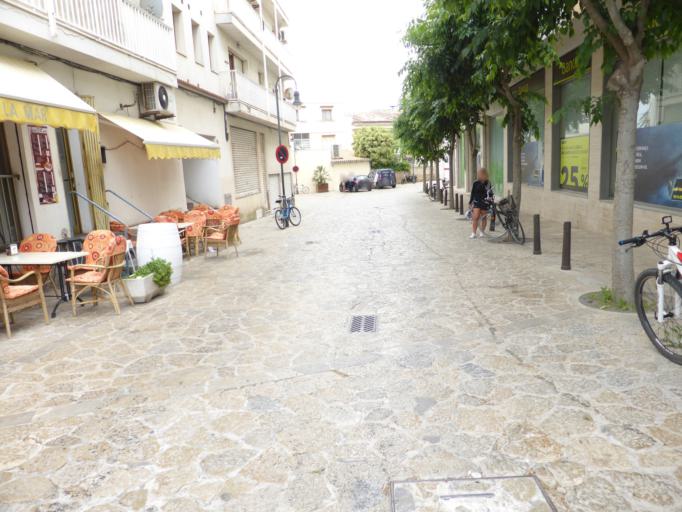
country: ES
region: Balearic Islands
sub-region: Illes Balears
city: Port d'Alcudia
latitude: 39.8420
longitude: 3.1355
